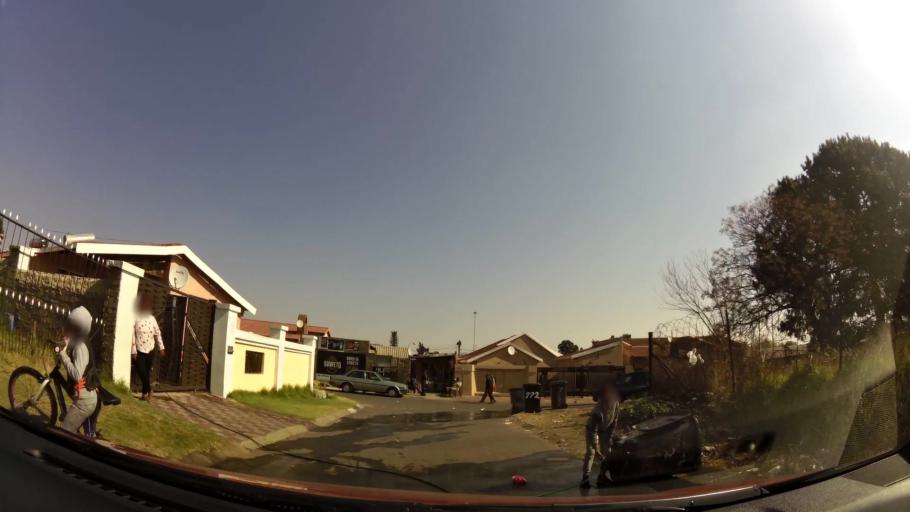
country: ZA
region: Gauteng
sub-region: City of Johannesburg Metropolitan Municipality
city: Soweto
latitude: -26.2416
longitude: 27.9416
